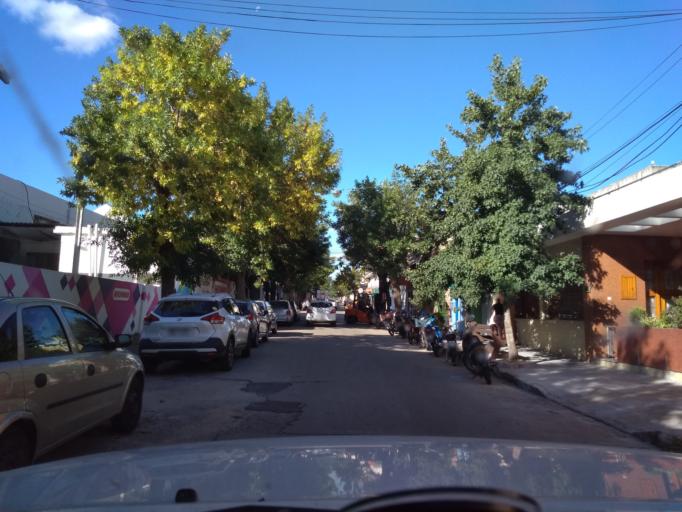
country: UY
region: Florida
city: Florida
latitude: -34.0975
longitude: -56.2175
